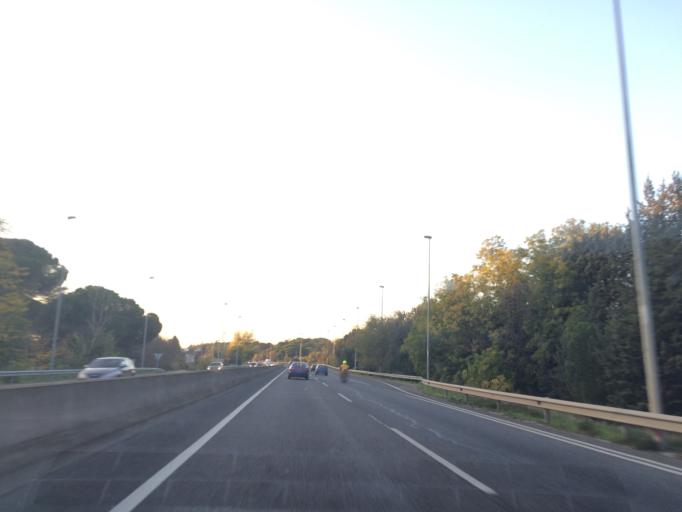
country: ES
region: Madrid
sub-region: Provincia de Madrid
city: Moncloa-Aravaca
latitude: 40.4415
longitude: -3.7467
